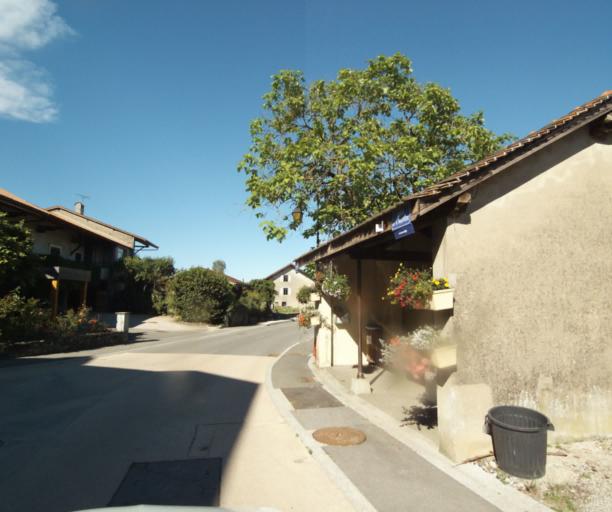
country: FR
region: Rhone-Alpes
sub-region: Departement de la Haute-Savoie
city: Massongy
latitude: 46.3494
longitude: 6.3301
